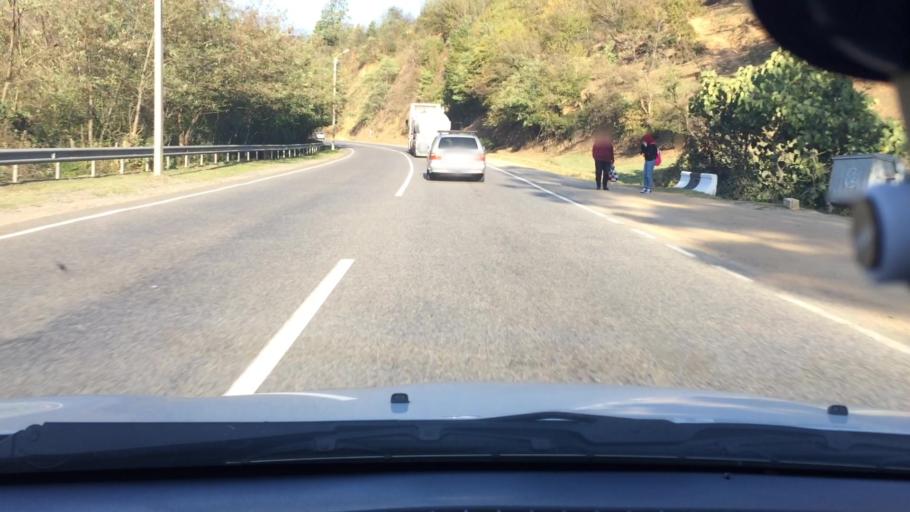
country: GE
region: Imereti
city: Kharagauli
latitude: 42.1082
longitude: 43.2609
